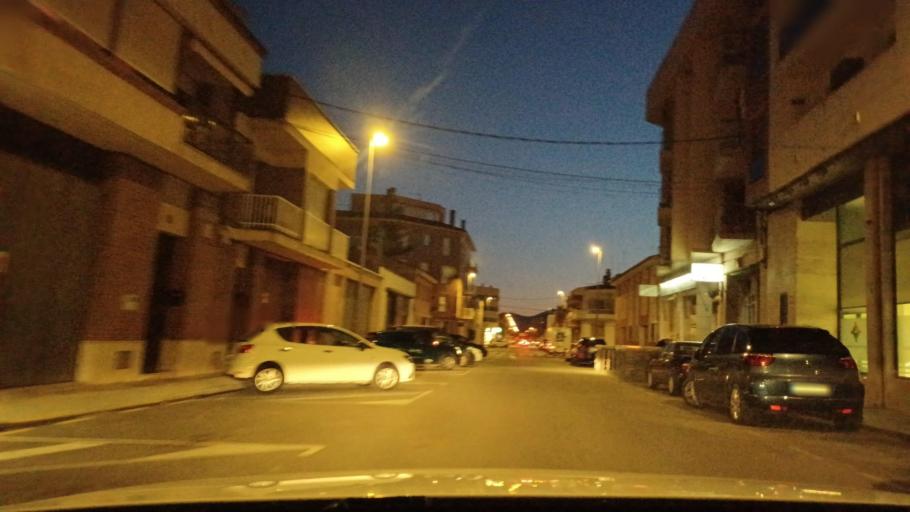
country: ES
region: Catalonia
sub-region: Provincia de Tarragona
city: Amposta
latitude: 40.7078
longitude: 0.5753
